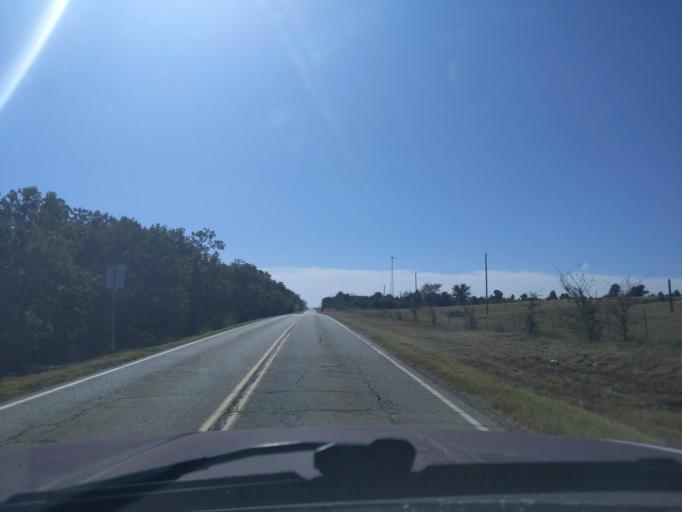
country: US
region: Oklahoma
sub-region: Creek County
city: Bristow
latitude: 35.7291
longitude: -96.3872
